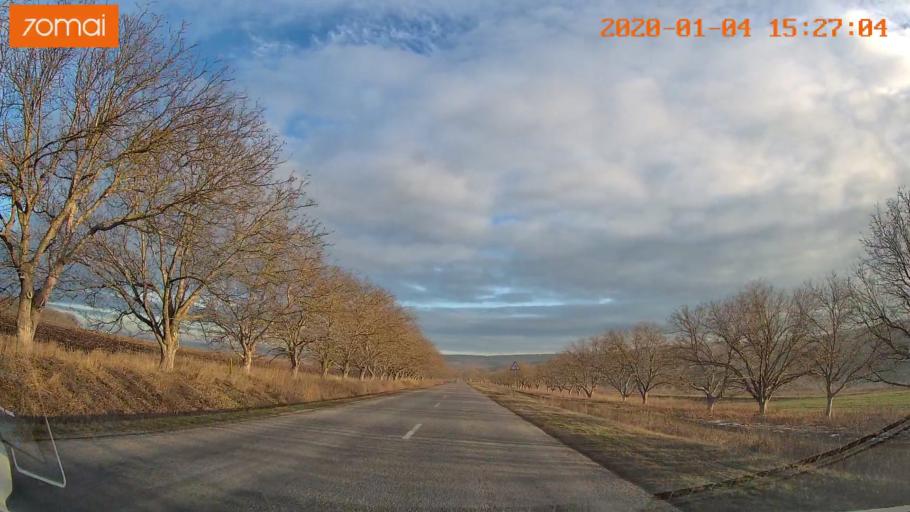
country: MD
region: Orhei
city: Orhei
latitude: 47.2869
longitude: 28.8227
